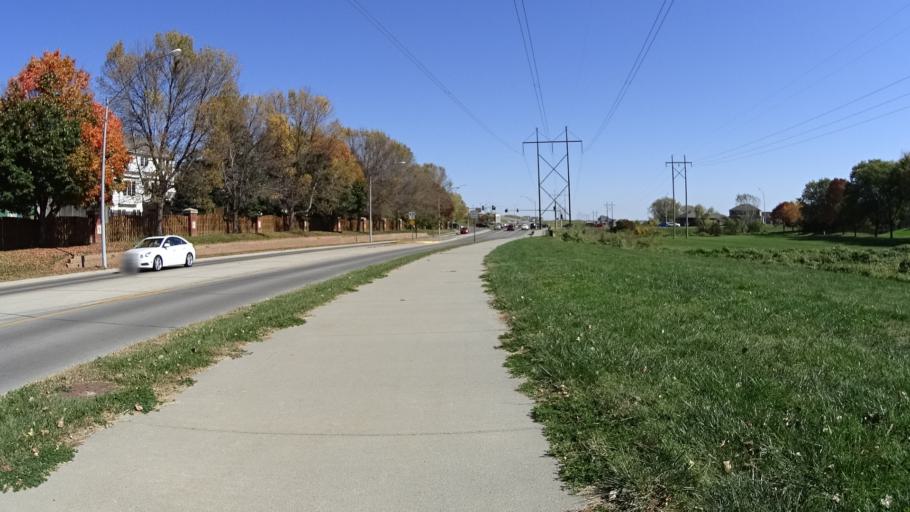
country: US
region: Nebraska
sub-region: Sarpy County
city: La Vista
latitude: 41.1692
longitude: -96.0258
